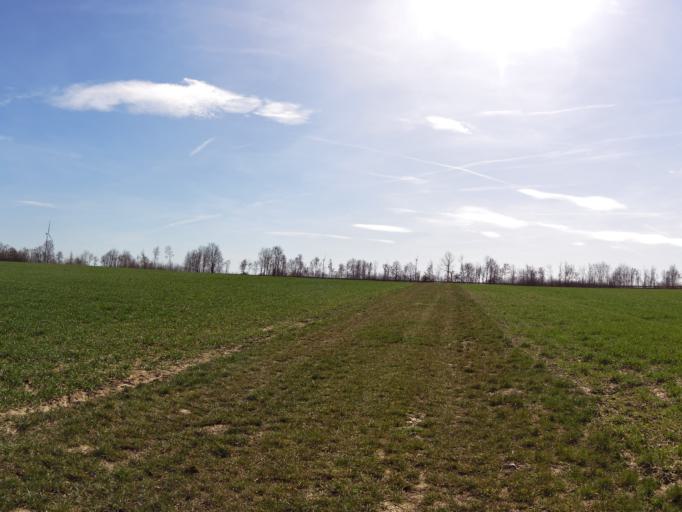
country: DE
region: Bavaria
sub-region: Regierungsbezirk Unterfranken
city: Biebelried
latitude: 49.7900
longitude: 10.0986
